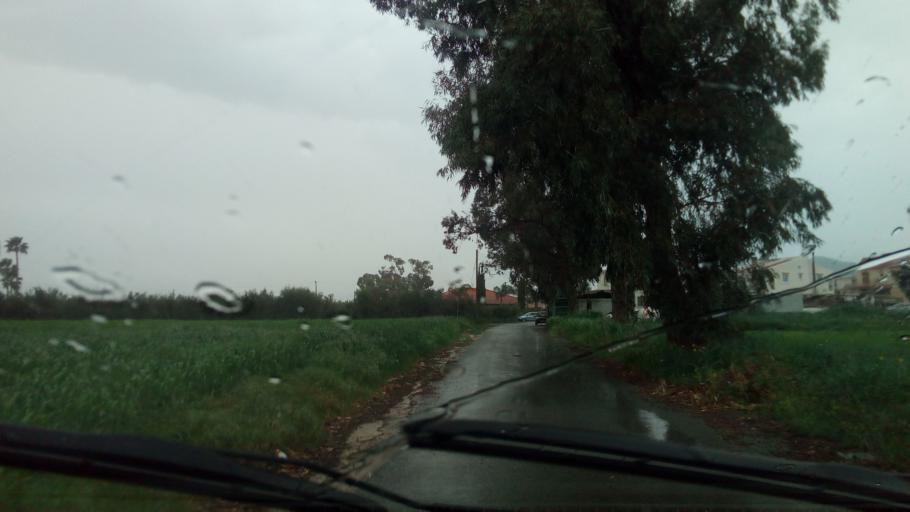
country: CY
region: Larnaka
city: Kofinou
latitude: 34.8468
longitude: 33.4633
